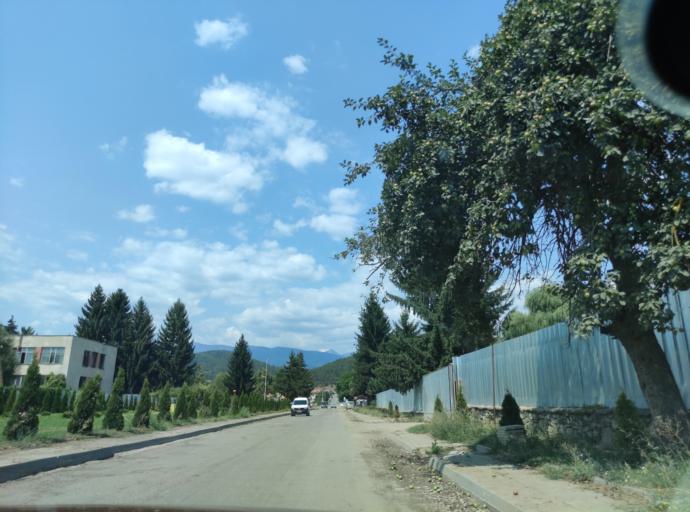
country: BG
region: Blagoevgrad
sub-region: Obshtina Belitsa
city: Belitsa
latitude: 41.9425
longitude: 23.5663
